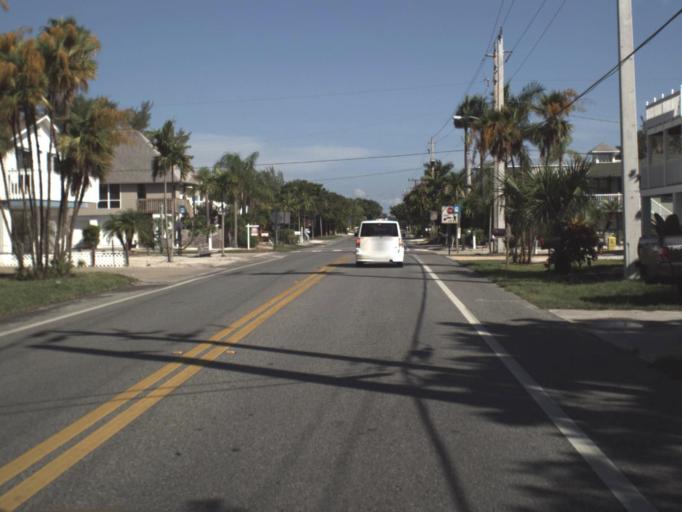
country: US
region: Florida
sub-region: Manatee County
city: Holmes Beach
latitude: 27.4858
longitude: -82.7058
